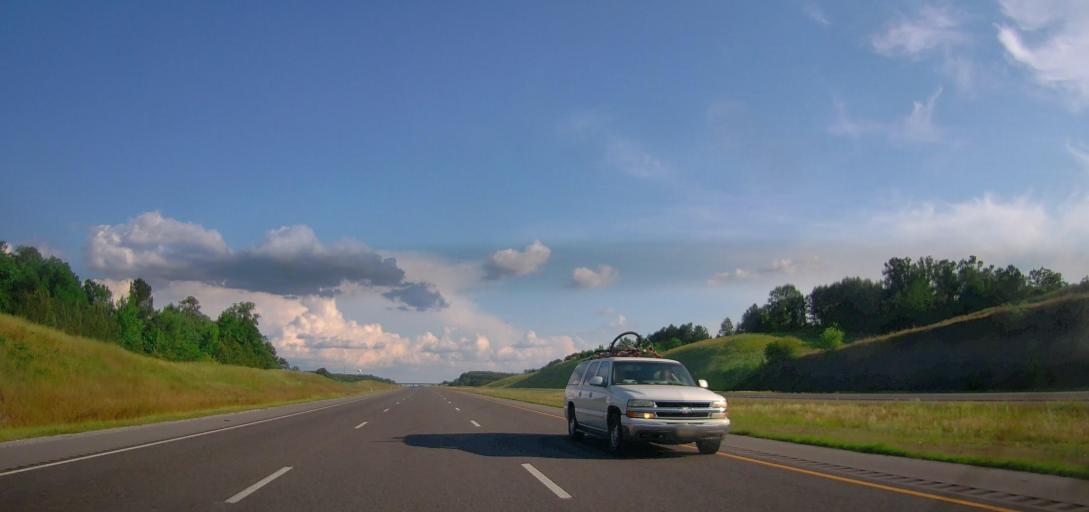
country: US
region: Alabama
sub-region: Walker County
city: Cordova
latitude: 33.7653
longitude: -87.2069
